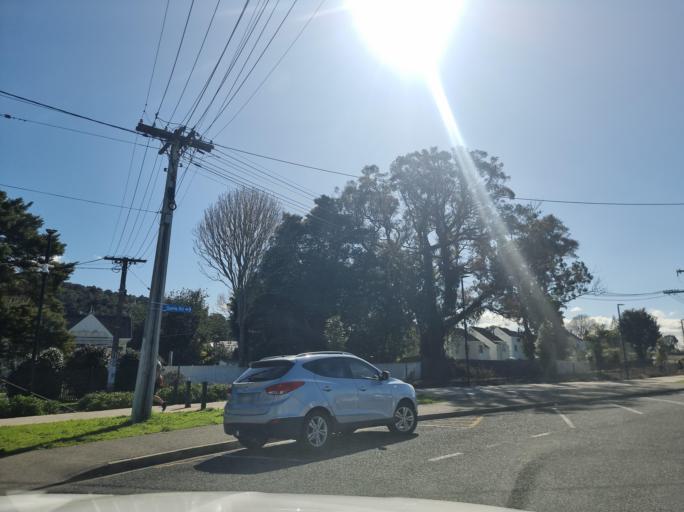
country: NZ
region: Northland
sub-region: Whangarei
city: Whangarei
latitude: -35.7164
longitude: 174.3208
